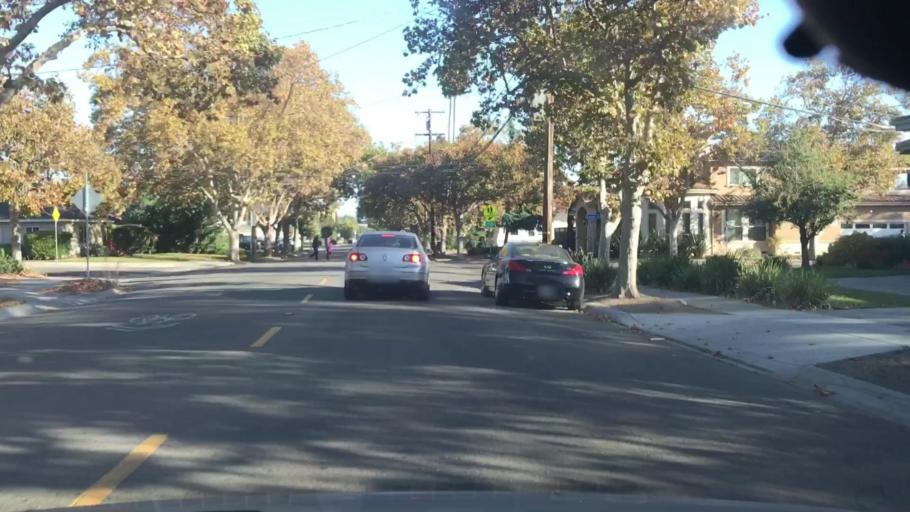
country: US
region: California
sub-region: Santa Clara County
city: Cupertino
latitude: 37.3191
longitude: -122.0065
